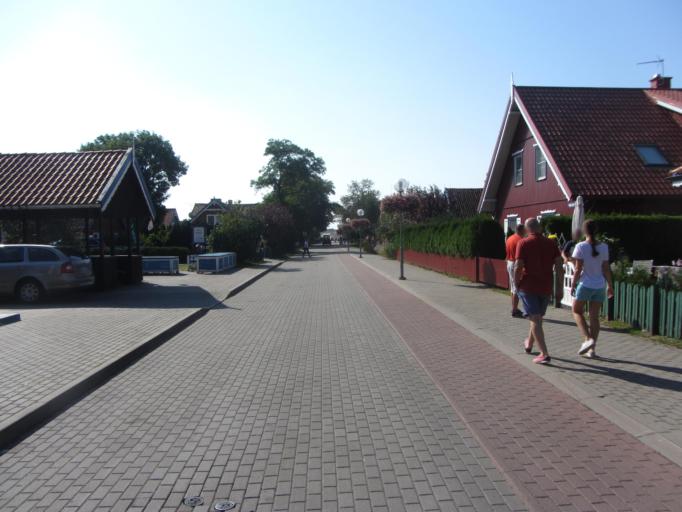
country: LT
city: Nida
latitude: 55.3031
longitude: 21.0069
